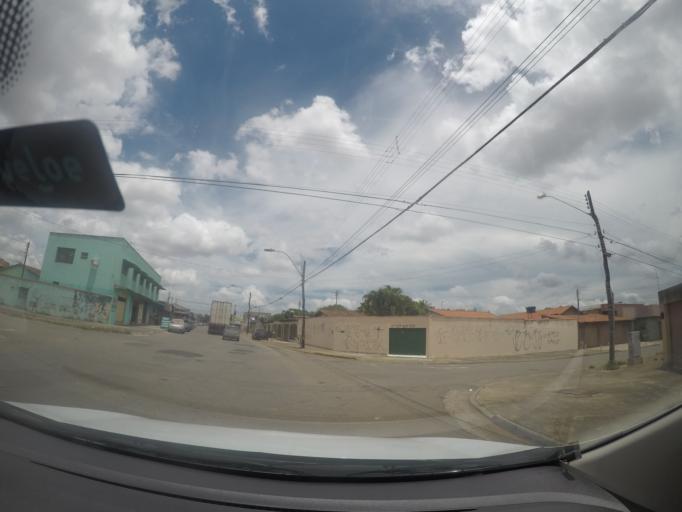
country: BR
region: Goias
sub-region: Goiania
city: Goiania
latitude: -16.6754
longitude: -49.3142
